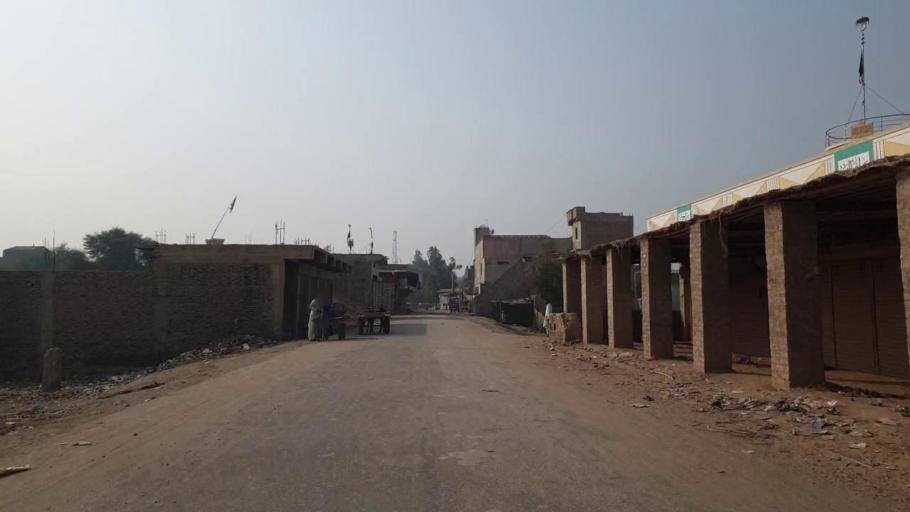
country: PK
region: Sindh
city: Sehwan
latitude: 26.4285
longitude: 67.8563
